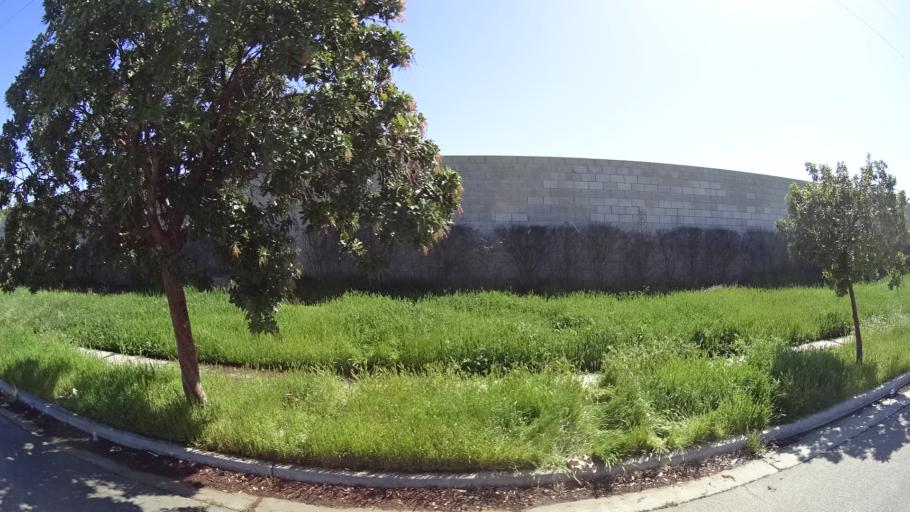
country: US
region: California
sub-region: Fresno County
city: Biola
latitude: 36.8157
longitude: -119.9009
